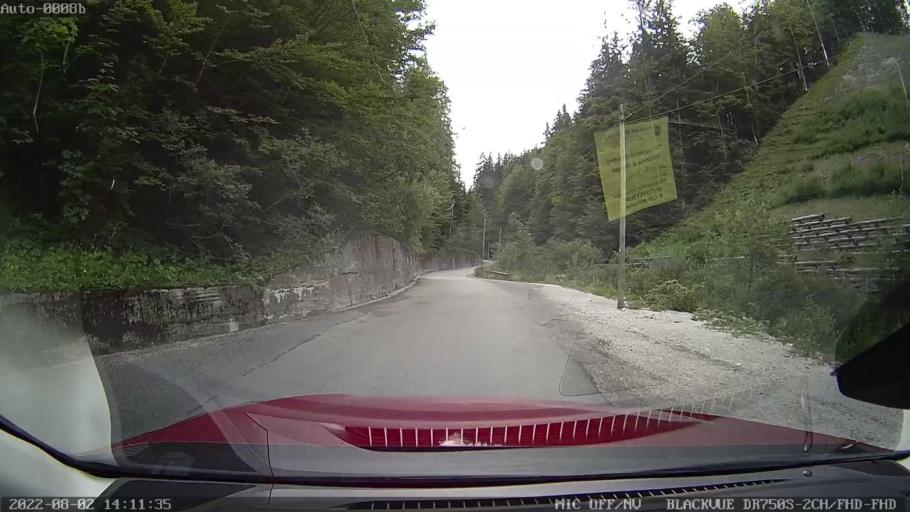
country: AT
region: Carinthia
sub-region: Politischer Bezirk Villach Land
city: Arnoldstein
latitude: 46.4854
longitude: 13.6742
